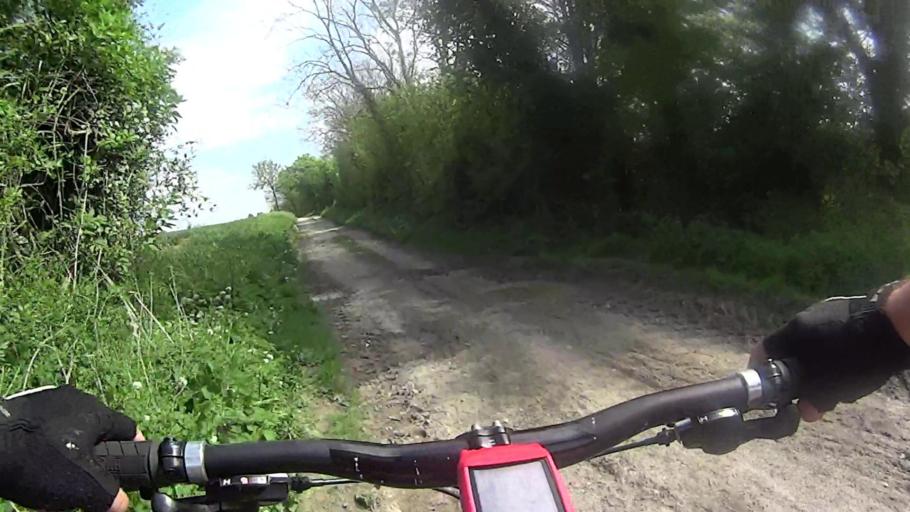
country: GB
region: England
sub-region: Hampshire
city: Petersfield
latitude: 50.9652
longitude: -0.9006
